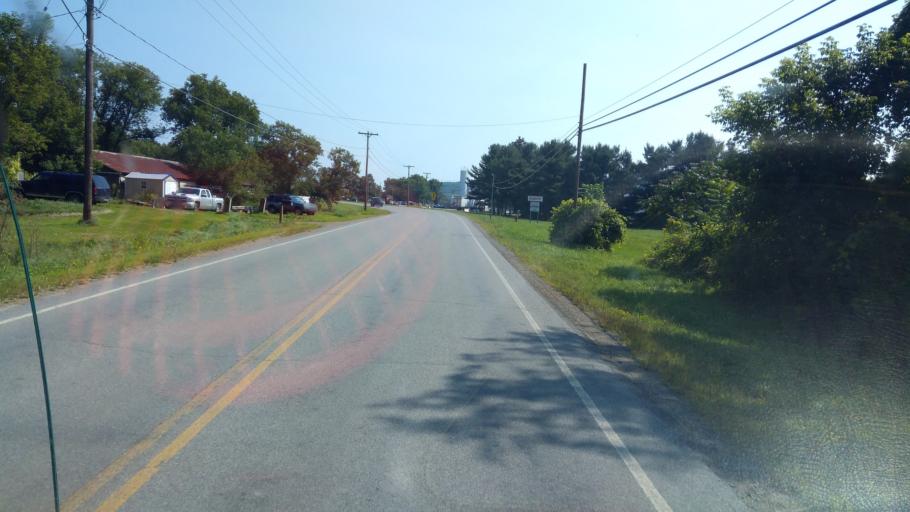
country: US
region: New York
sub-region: Allegany County
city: Friendship
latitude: 42.2136
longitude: -78.1196
